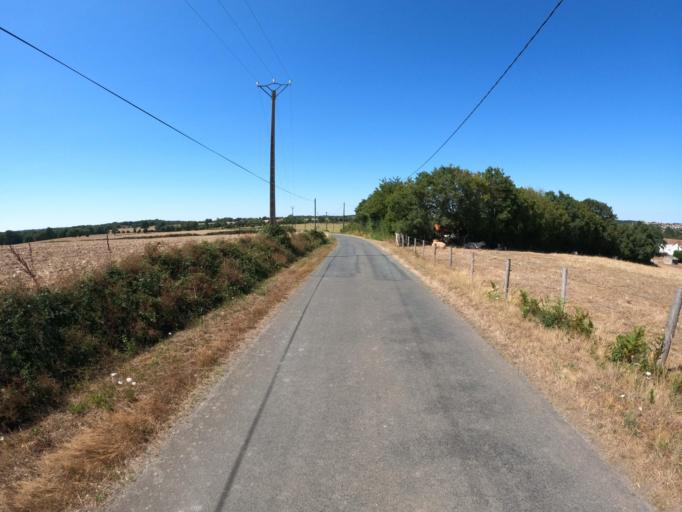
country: FR
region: Pays de la Loire
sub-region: Departement de Maine-et-Loire
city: Saint-Christophe-du-Bois
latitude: 47.0458
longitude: -0.9571
